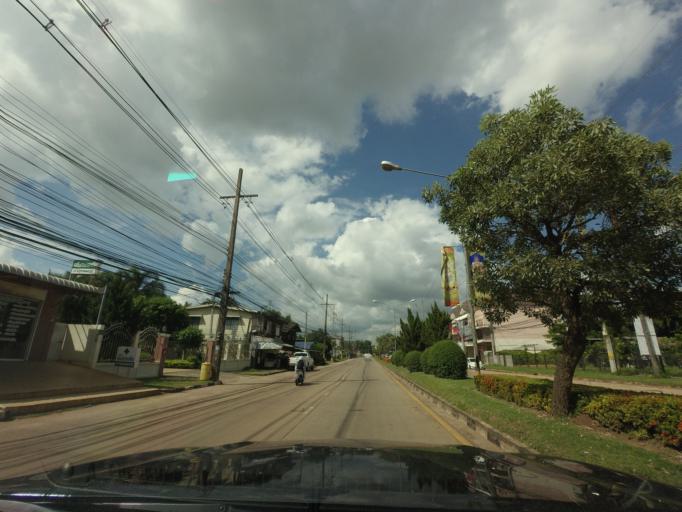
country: TH
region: Changwat Udon Thani
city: Udon Thani
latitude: 17.4315
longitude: 102.7774
